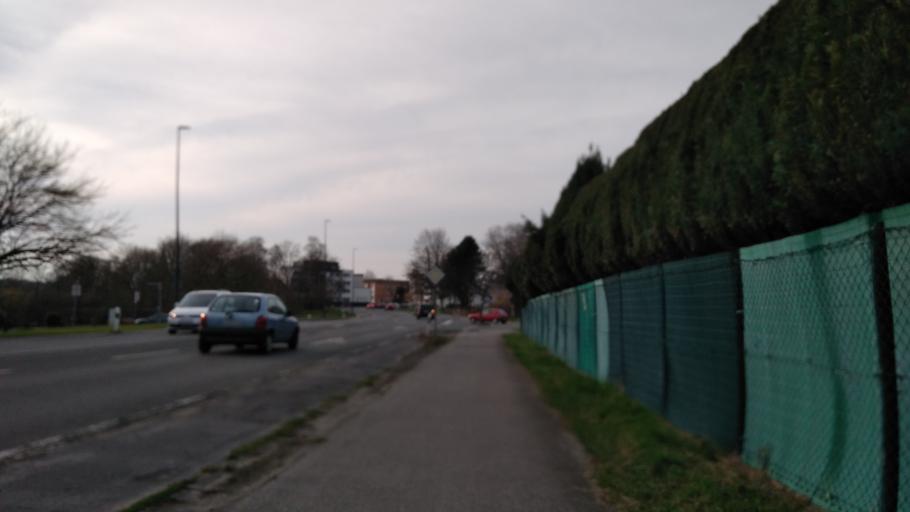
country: DE
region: North Rhine-Westphalia
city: Herten
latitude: 51.5988
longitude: 7.1023
